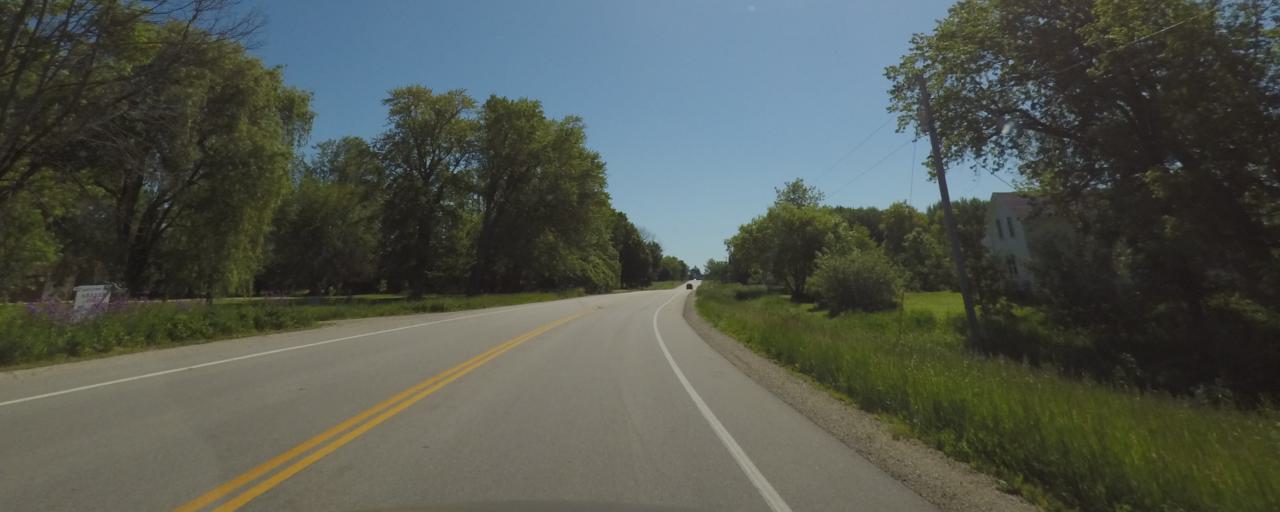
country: US
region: Wisconsin
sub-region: Sheboygan County
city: Plymouth
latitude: 43.7468
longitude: -87.9124
